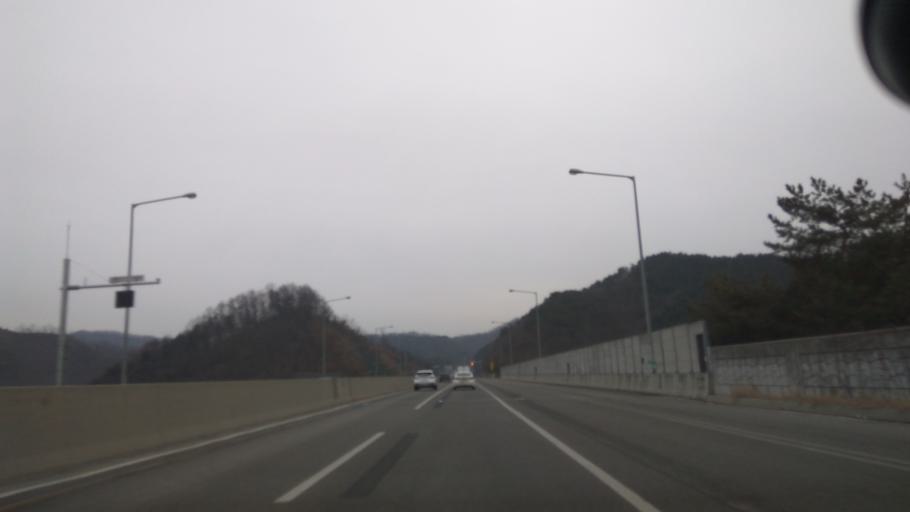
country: KR
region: Gangwon-do
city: Sindong
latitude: 37.7343
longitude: 127.6238
